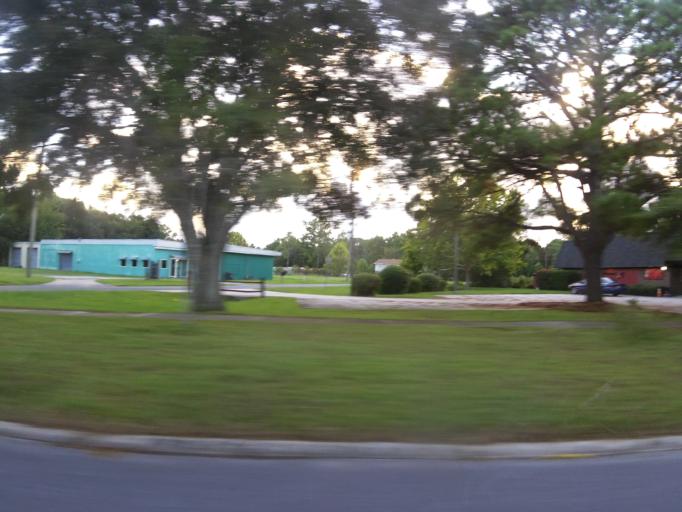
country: US
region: Georgia
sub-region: Camden County
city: St. Marys
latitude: 30.7366
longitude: -81.5455
